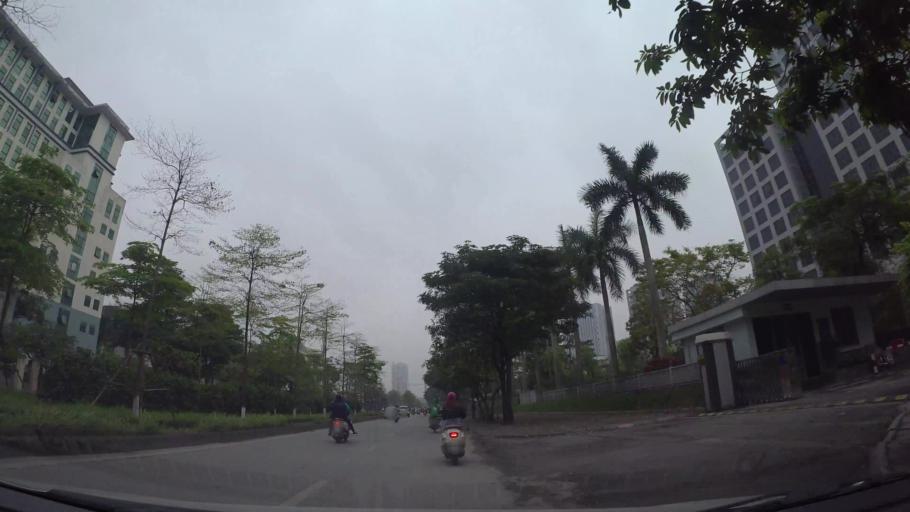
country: VN
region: Ha Noi
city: Cau Giay
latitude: 21.0282
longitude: 105.7829
